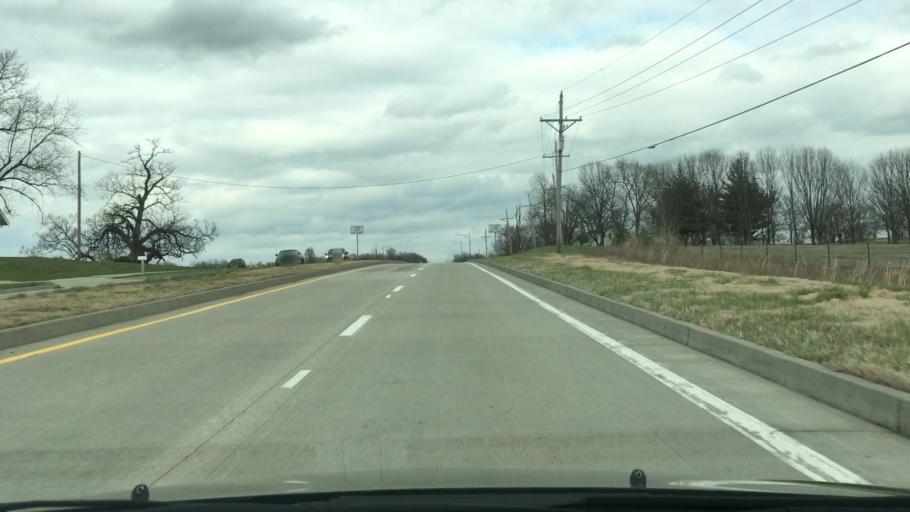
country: US
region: Missouri
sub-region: Cass County
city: Raymore
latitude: 38.8548
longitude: -94.4527
